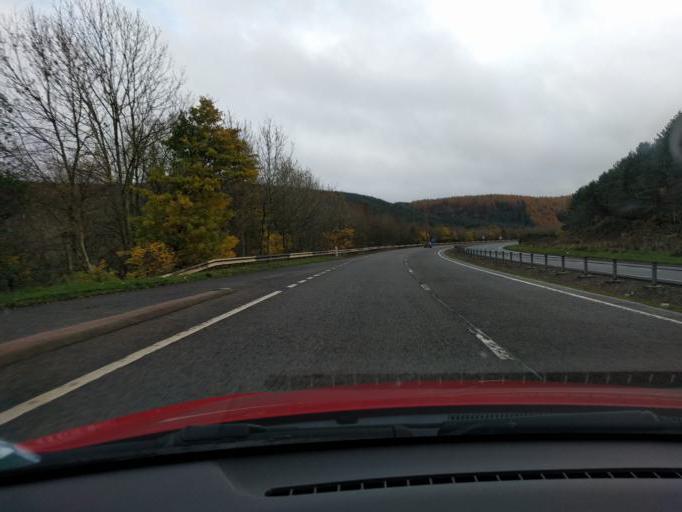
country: GB
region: Scotland
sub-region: The Scottish Borders
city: Duns
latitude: 55.9043
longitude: -2.3283
